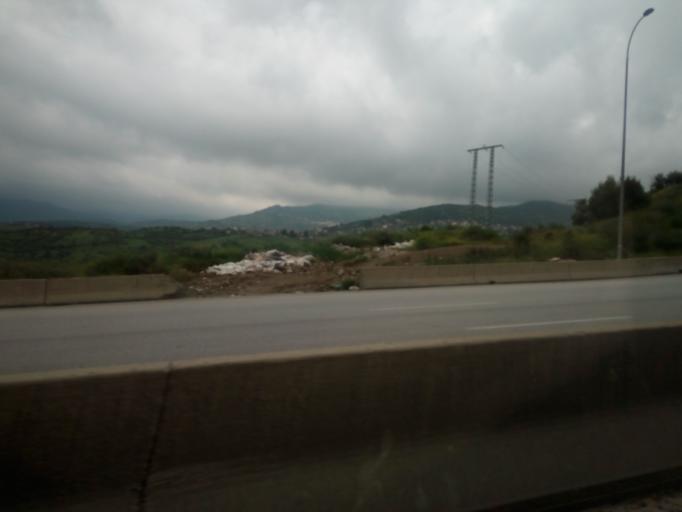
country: DZ
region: Bouira
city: Lakhdaria
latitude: 36.5894
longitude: 3.5267
